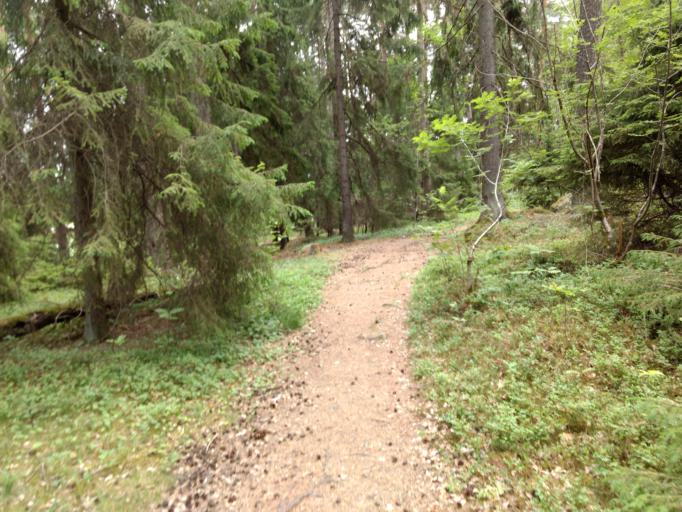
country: SE
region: Stockholm
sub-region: Upplands Vasby Kommun
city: Upplands Vaesby
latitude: 59.5322
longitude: 17.9165
